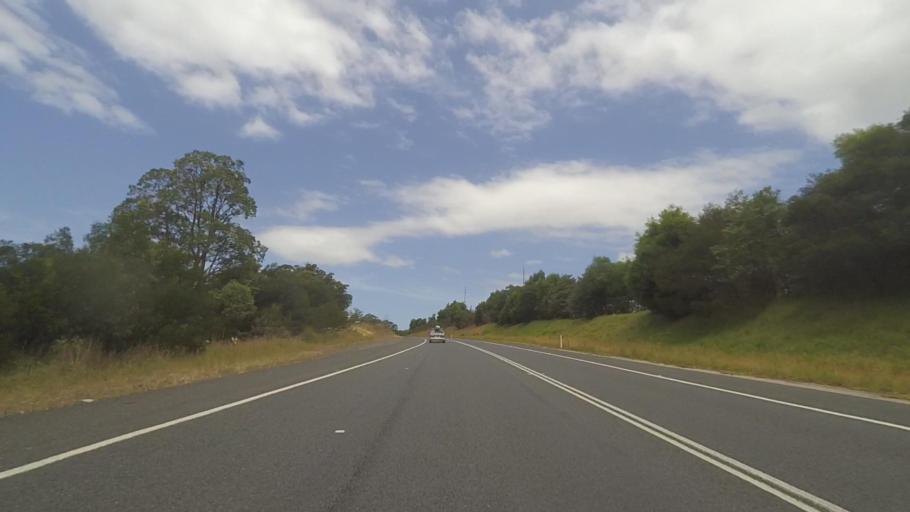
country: AU
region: New South Wales
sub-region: Shoalhaven Shire
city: Milton
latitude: -35.2192
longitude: 150.4349
